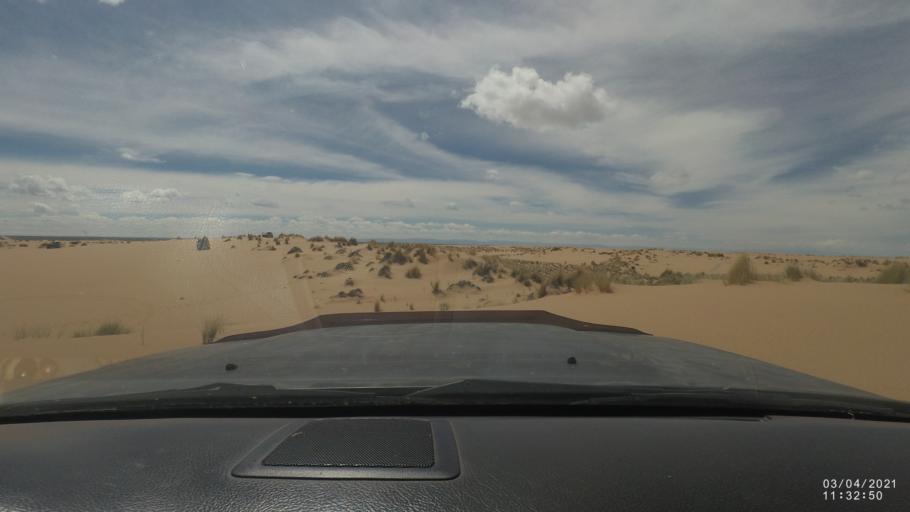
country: BO
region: Oruro
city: Poopo
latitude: -18.7024
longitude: -67.5062
